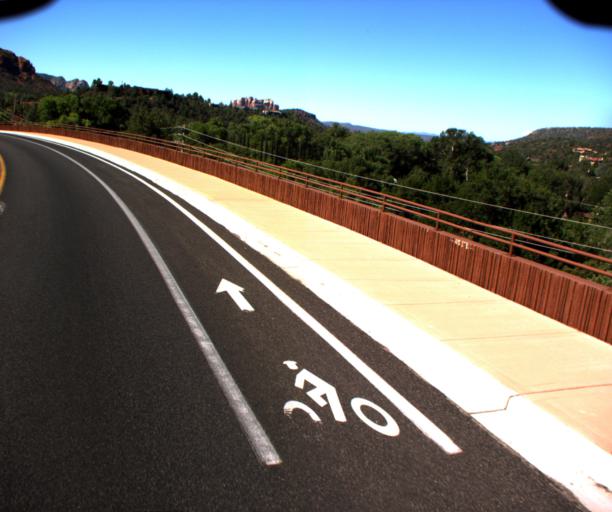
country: US
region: Arizona
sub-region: Coconino County
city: Sedona
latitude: 34.8552
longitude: -111.7642
